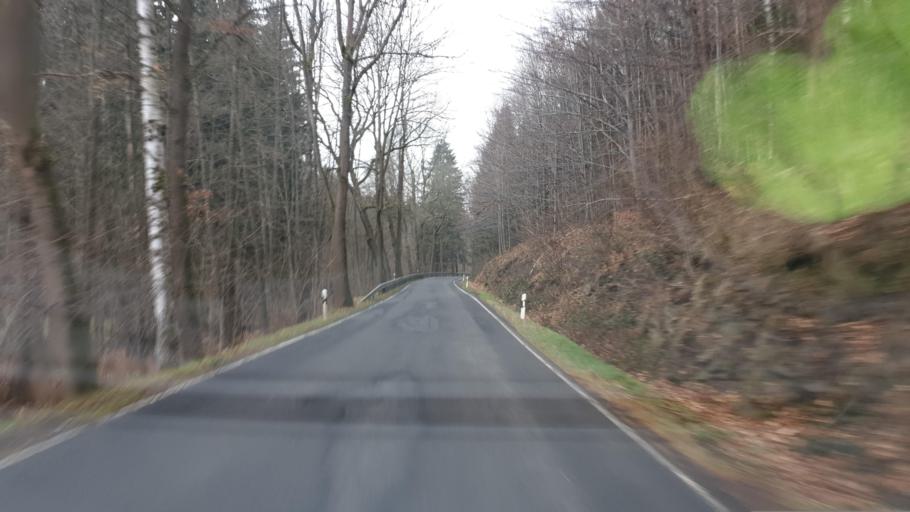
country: DE
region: Saxony
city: Mulda
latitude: 50.7822
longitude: 13.4222
